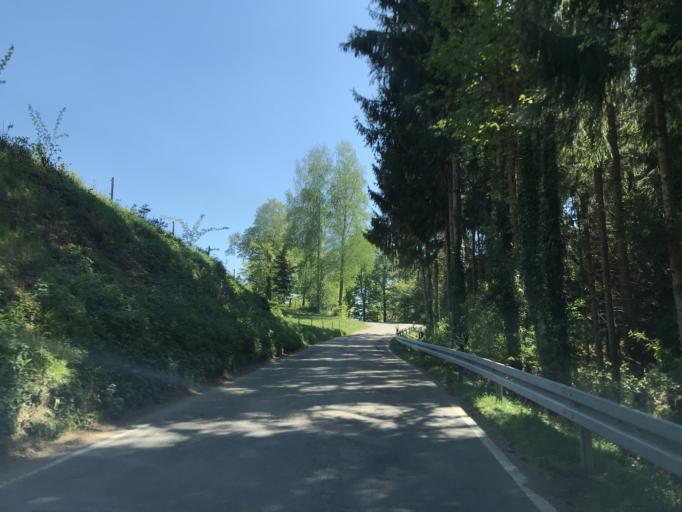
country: DE
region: Baden-Wuerttemberg
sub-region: Freiburg Region
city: Hasel
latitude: 47.6790
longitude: 7.8755
